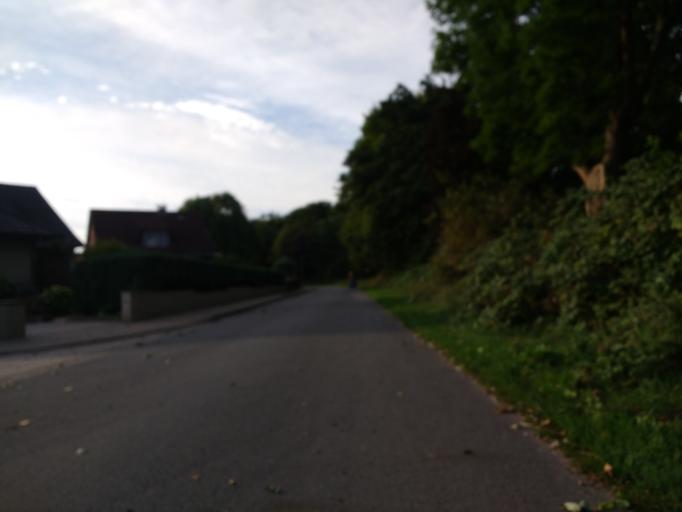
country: DE
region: Lower Saxony
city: Isenbuttel
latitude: 52.4400
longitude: 10.5673
